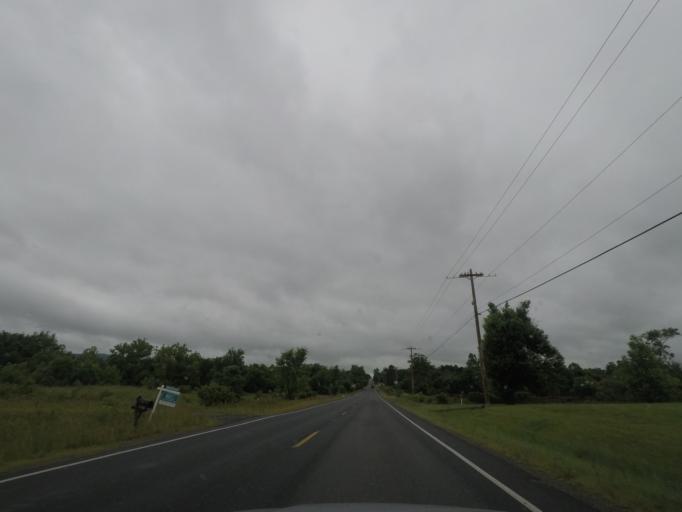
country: US
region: Virginia
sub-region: Prince William County
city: Bull Run Mountain Estates
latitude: 38.8866
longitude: -77.6327
